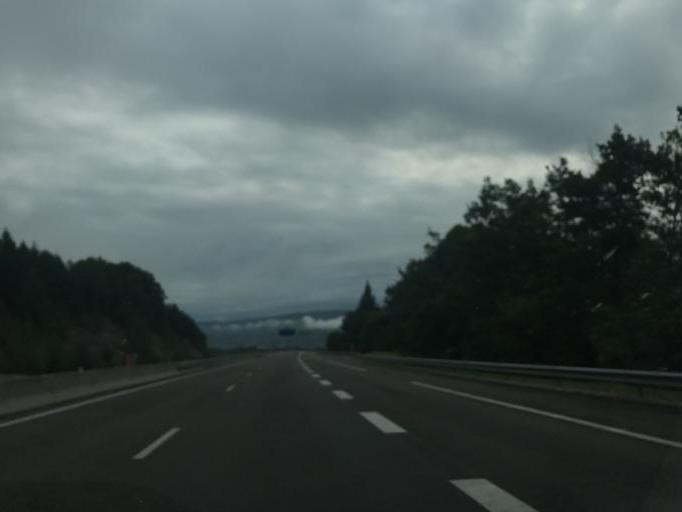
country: FR
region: Rhone-Alpes
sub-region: Departement de l'Ain
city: Oyonnax
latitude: 46.2669
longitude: 5.6422
